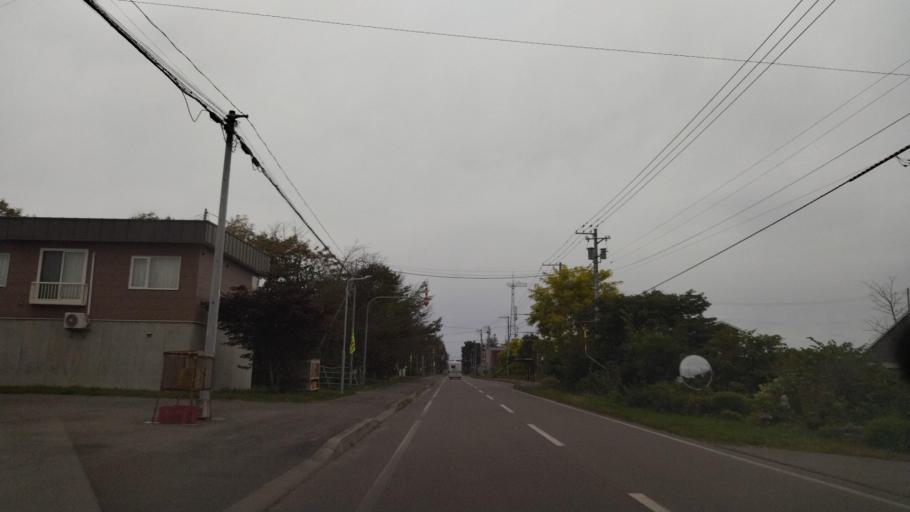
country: JP
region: Hokkaido
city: Otofuke
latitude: 43.2246
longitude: 143.2793
